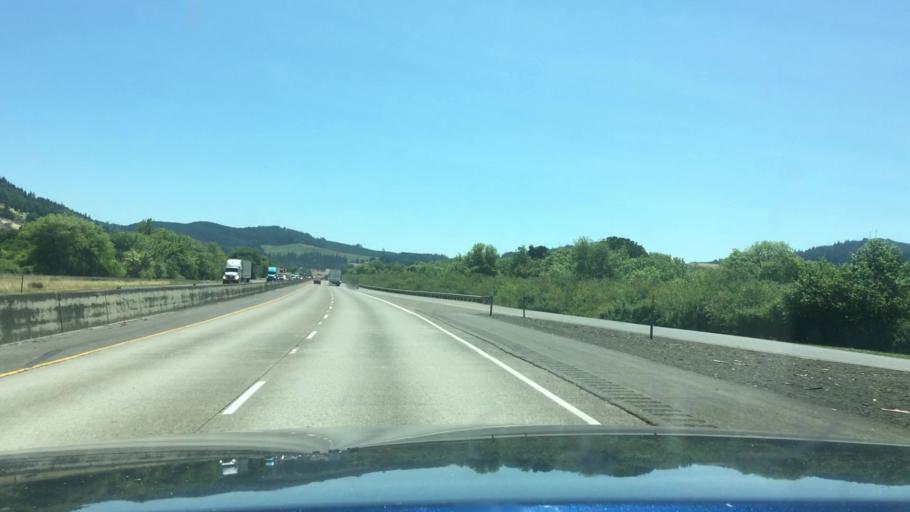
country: US
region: Oregon
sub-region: Douglas County
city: Yoncalla
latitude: 43.5619
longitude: -123.2810
